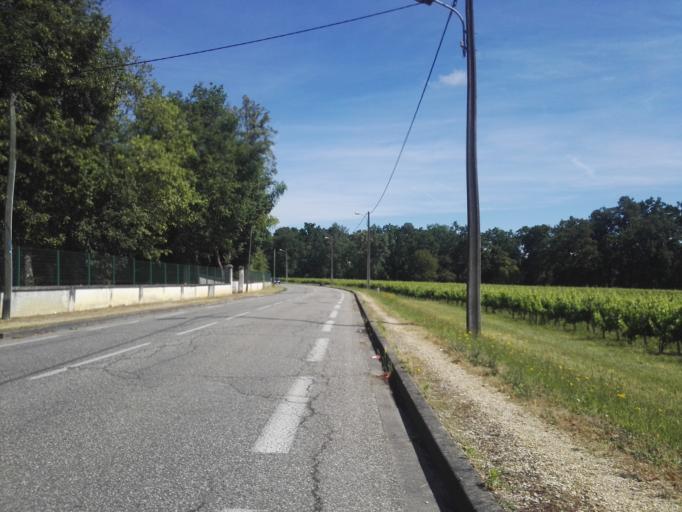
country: FR
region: Aquitaine
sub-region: Departement de la Gironde
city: Leognan
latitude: 44.7465
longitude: -0.5871
